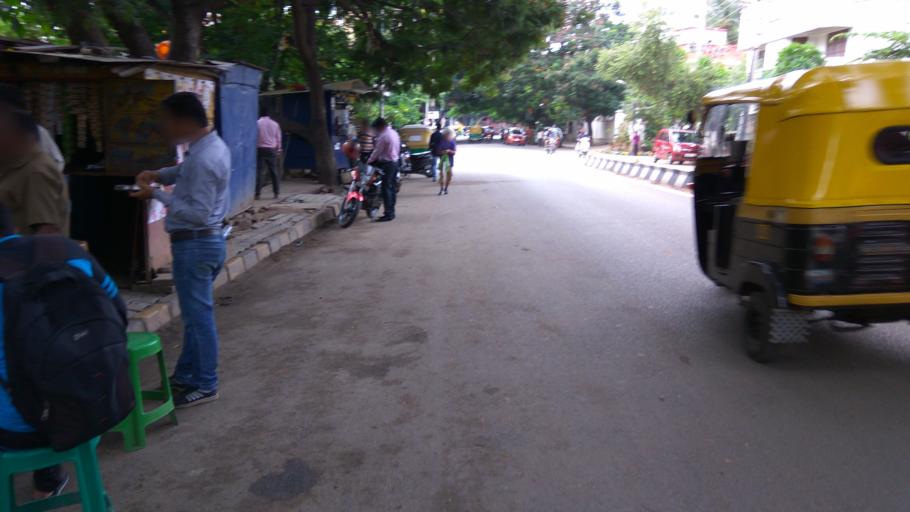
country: IN
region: Karnataka
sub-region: Bangalore Urban
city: Bangalore
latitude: 12.9638
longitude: 77.6406
